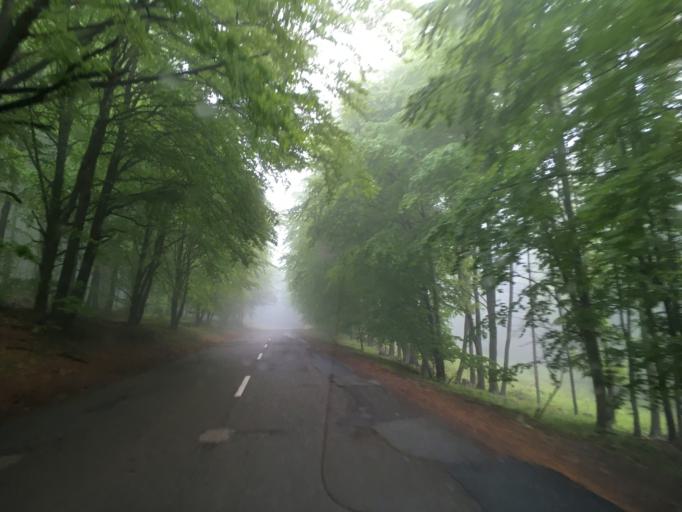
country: HU
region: Heves
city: Paradsasvar
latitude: 47.8689
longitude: 20.0004
